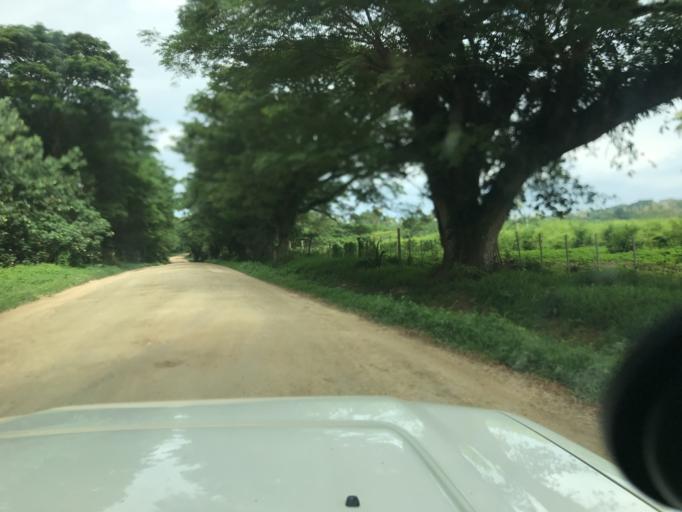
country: VU
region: Sanma
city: Luganville
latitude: -15.5581
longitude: 167.1370
